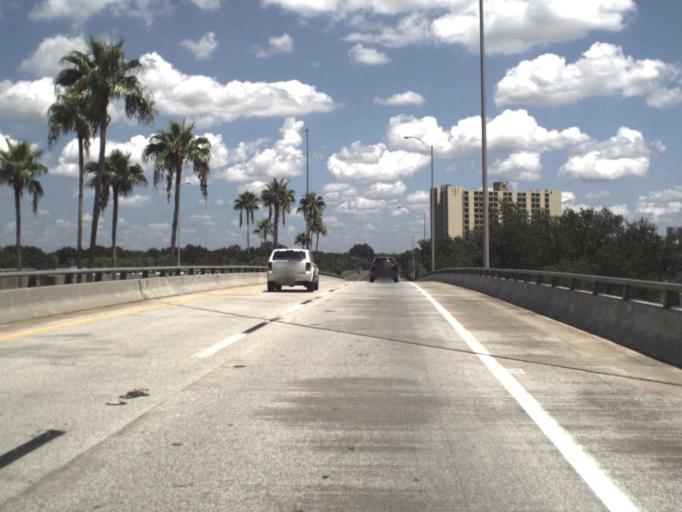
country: US
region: Florida
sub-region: Hillsborough County
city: Tampa
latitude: 27.9186
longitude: -82.4934
